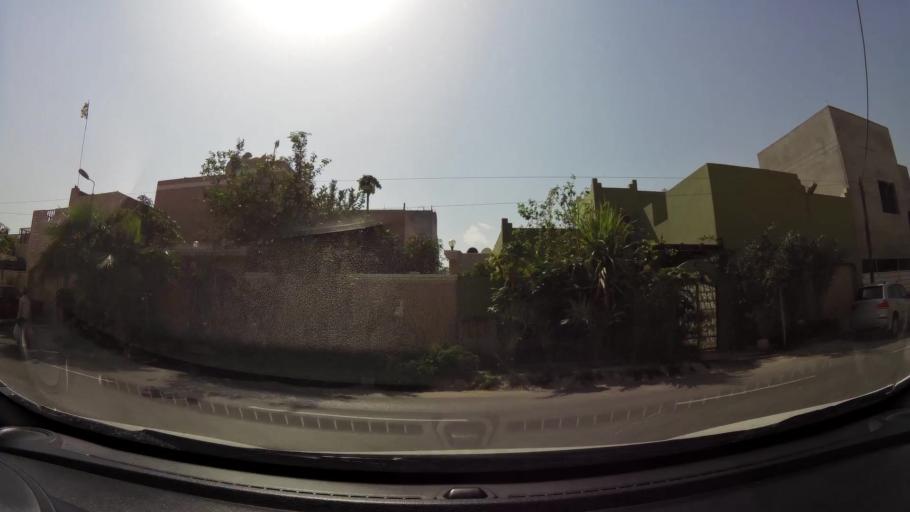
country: BH
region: Manama
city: Jidd Hafs
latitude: 26.2073
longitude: 50.4647
